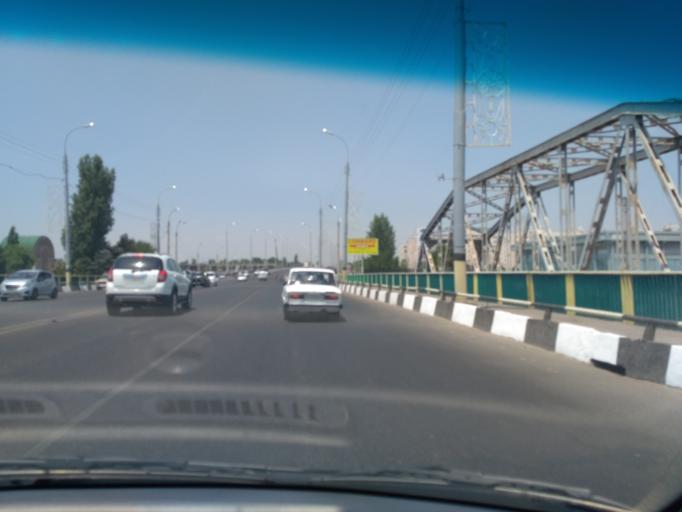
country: UZ
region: Toshkent Shahri
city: Bektemir
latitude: 41.2354
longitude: 69.3327
